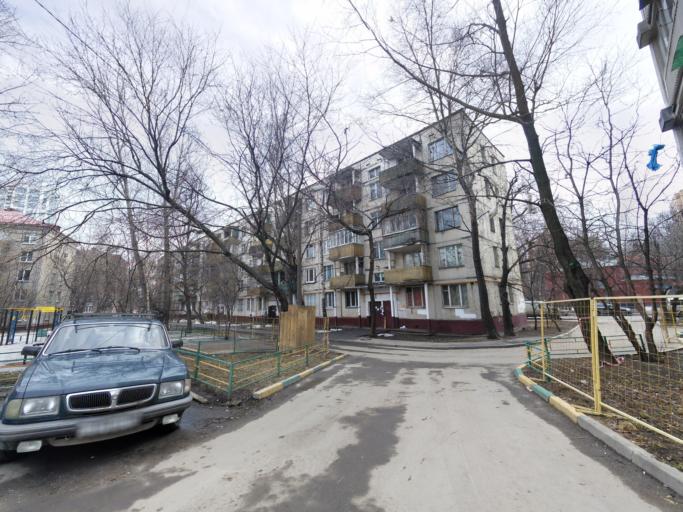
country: RU
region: Moscow
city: Sokol
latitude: 55.8075
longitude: 37.5360
